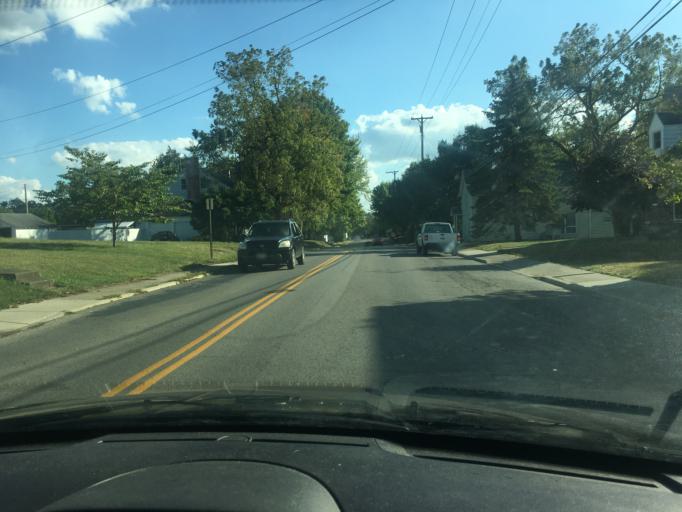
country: US
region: Ohio
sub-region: Logan County
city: Bellefontaine
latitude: 40.3615
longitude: -83.7488
